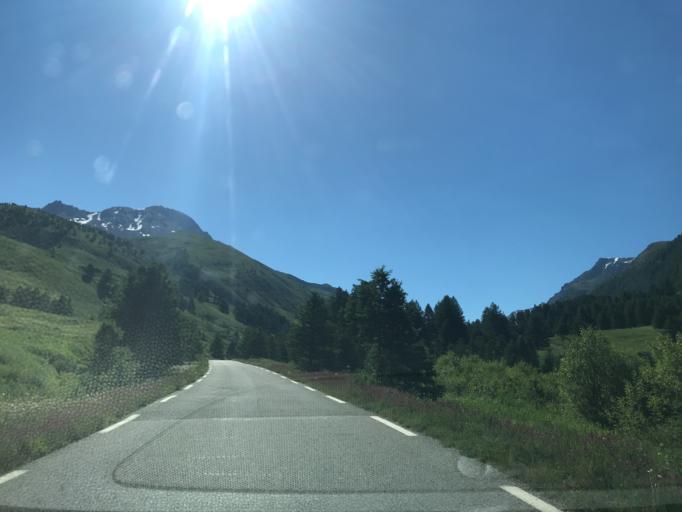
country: IT
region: Piedmont
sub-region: Provincia di Cuneo
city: Pontechianale
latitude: 44.7183
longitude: 6.9064
